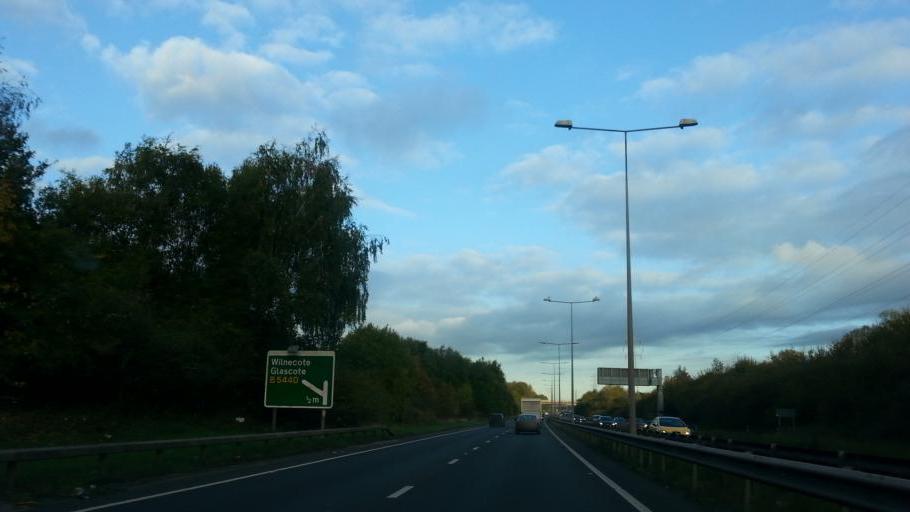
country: GB
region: England
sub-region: Staffordshire
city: Fazeley
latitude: 52.6111
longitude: -1.6584
